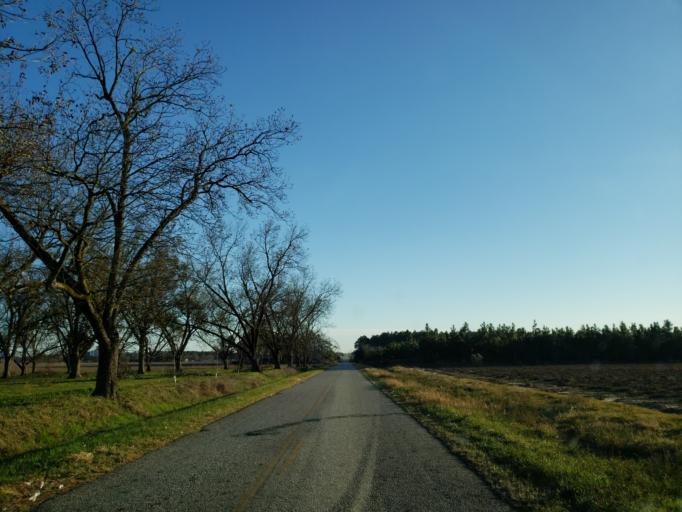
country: US
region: Georgia
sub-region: Dooly County
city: Vienna
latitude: 32.1539
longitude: -83.7608
